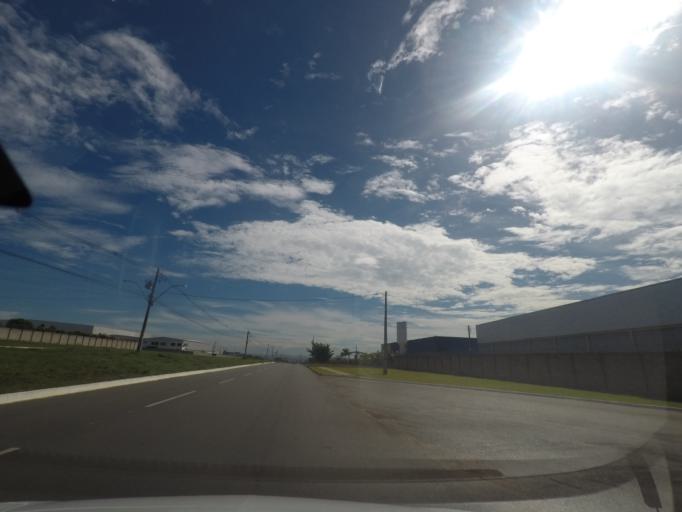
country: BR
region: Goias
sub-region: Aparecida De Goiania
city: Aparecida de Goiania
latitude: -16.8048
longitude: -49.2623
